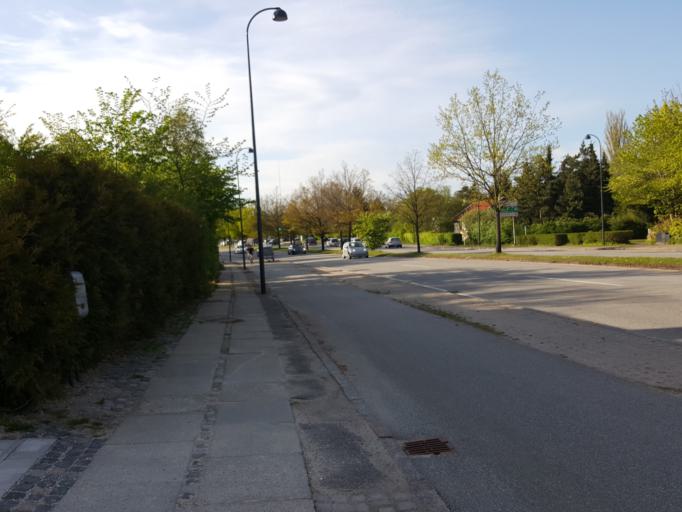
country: DK
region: Capital Region
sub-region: Rudersdal Kommune
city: Holte
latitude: 55.8212
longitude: 12.4657
